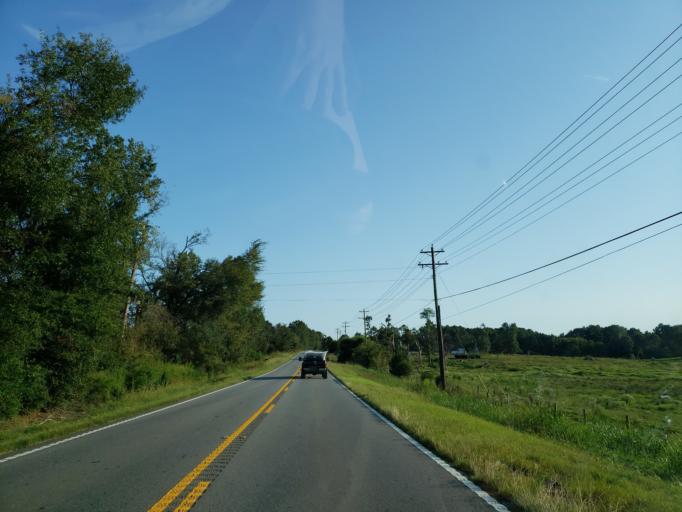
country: US
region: Georgia
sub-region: Murray County
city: Chatsworth
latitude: 34.8001
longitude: -84.8236
